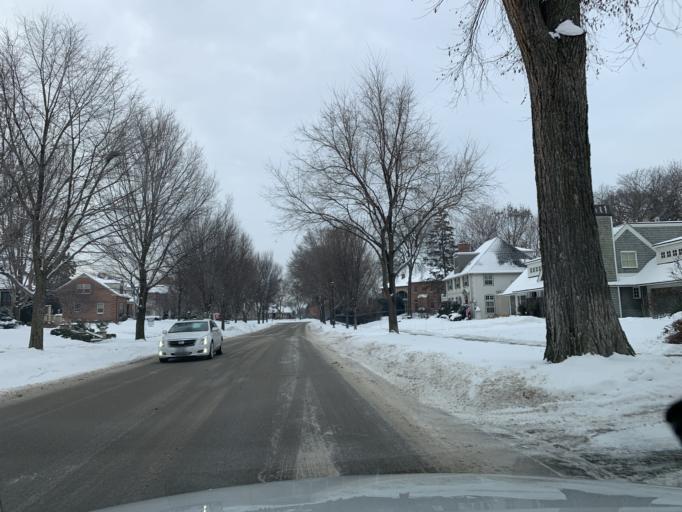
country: US
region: Minnesota
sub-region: Hennepin County
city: Edina
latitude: 44.9155
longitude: -93.3412
